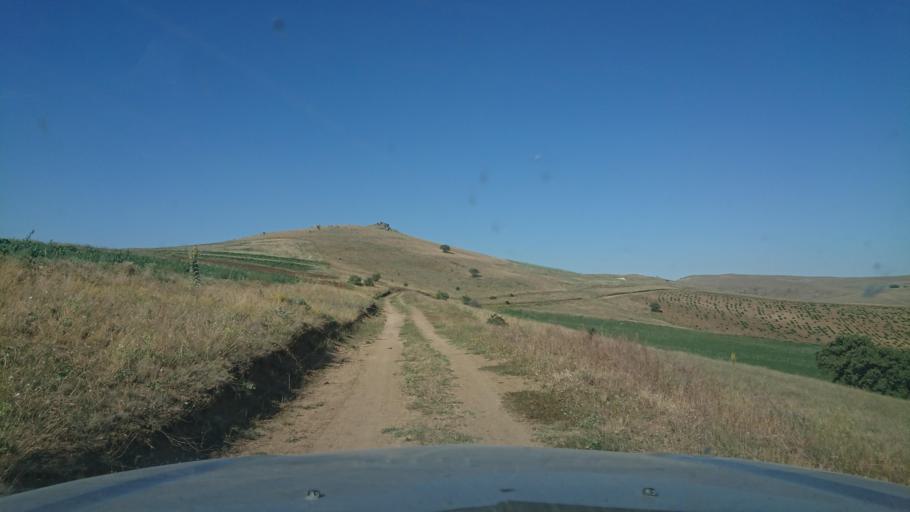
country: TR
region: Aksaray
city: Agacoren
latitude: 38.8364
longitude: 33.9358
